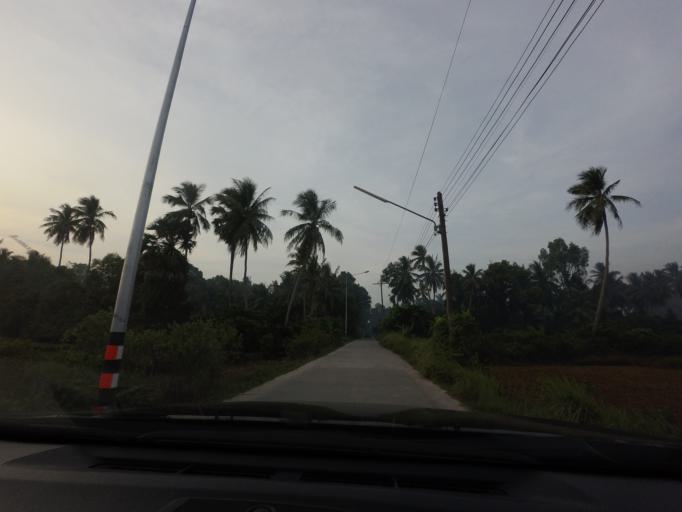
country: TH
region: Pattani
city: Yaring
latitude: 6.8624
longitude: 101.4042
